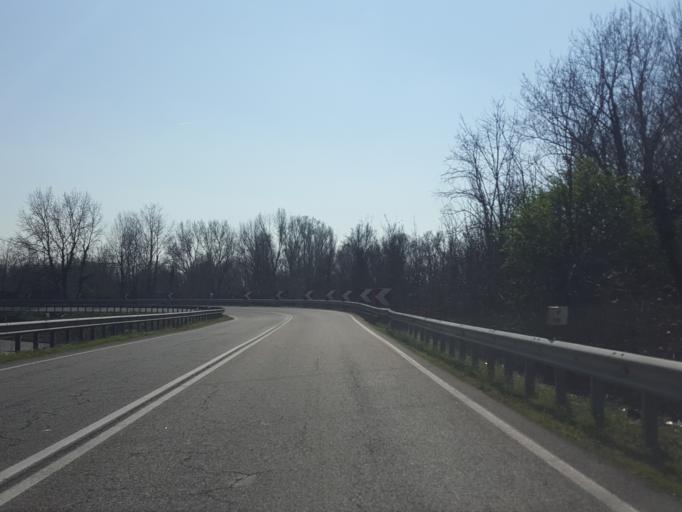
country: IT
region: Veneto
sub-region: Provincia di Padova
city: Fontaniva
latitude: 45.6326
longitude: 11.7382
